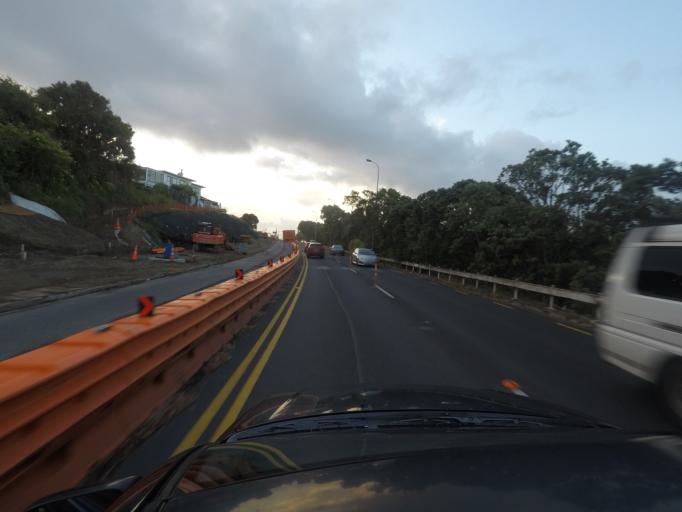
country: NZ
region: Auckland
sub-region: Auckland
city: Tamaki
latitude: -36.9044
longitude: 174.8550
